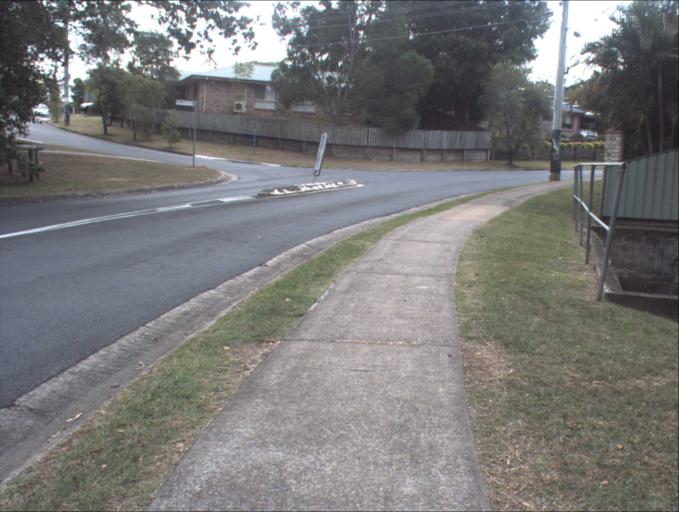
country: AU
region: Queensland
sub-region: Logan
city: Slacks Creek
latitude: -27.6391
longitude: 153.1581
